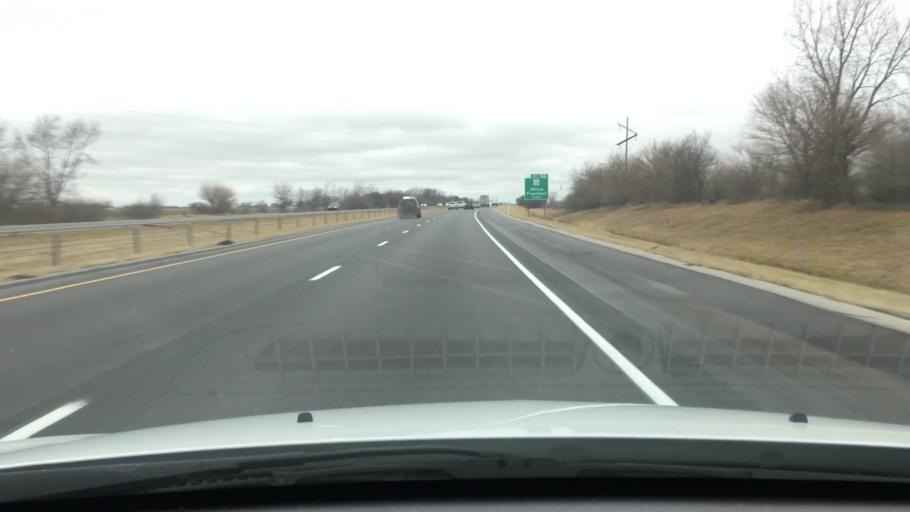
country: US
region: Indiana
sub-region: Clinton County
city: Mulberry
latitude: 40.2444
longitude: -86.6365
